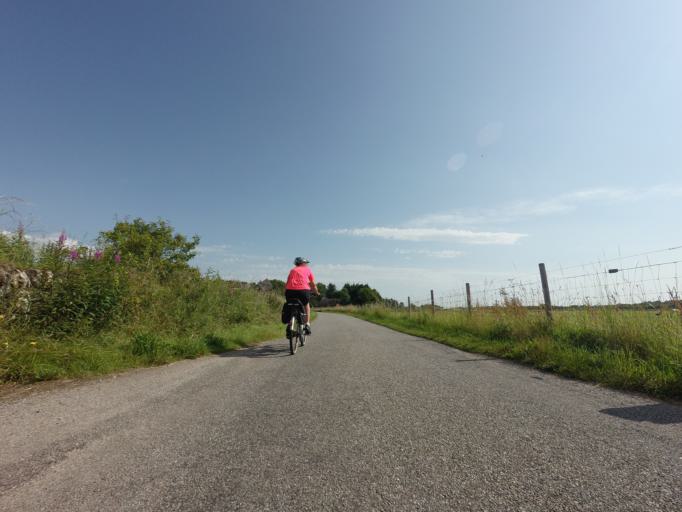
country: GB
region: Scotland
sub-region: Highland
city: Alness
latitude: 57.7111
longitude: -4.2241
